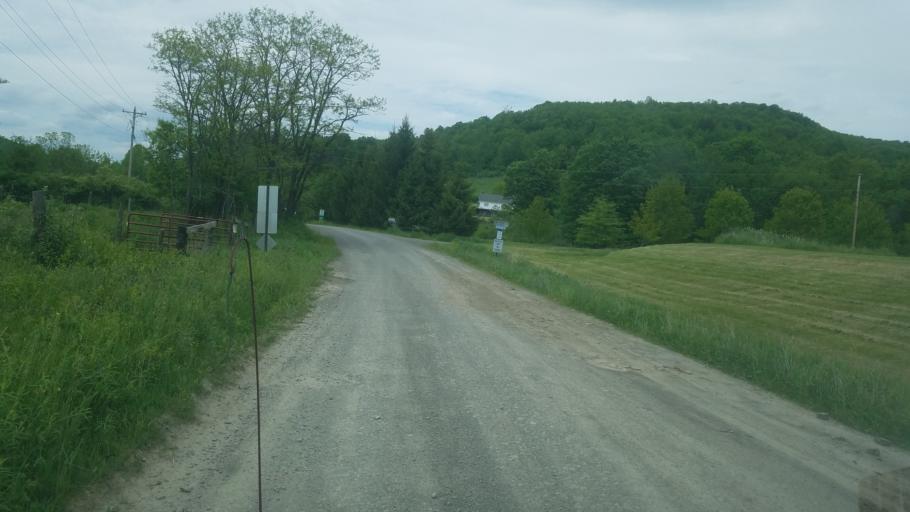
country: US
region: Pennsylvania
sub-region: Tioga County
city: Westfield
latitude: 41.8823
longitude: -77.5961
